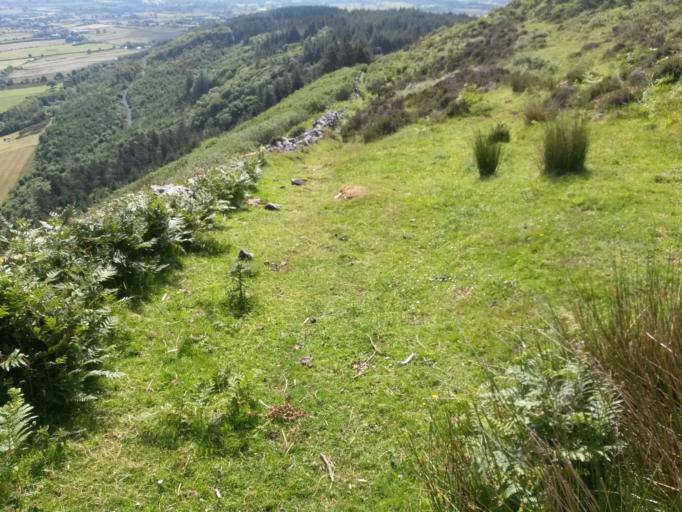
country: IE
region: Connaught
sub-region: Sligo
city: Strandhill
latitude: 54.2625
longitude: -8.5715
